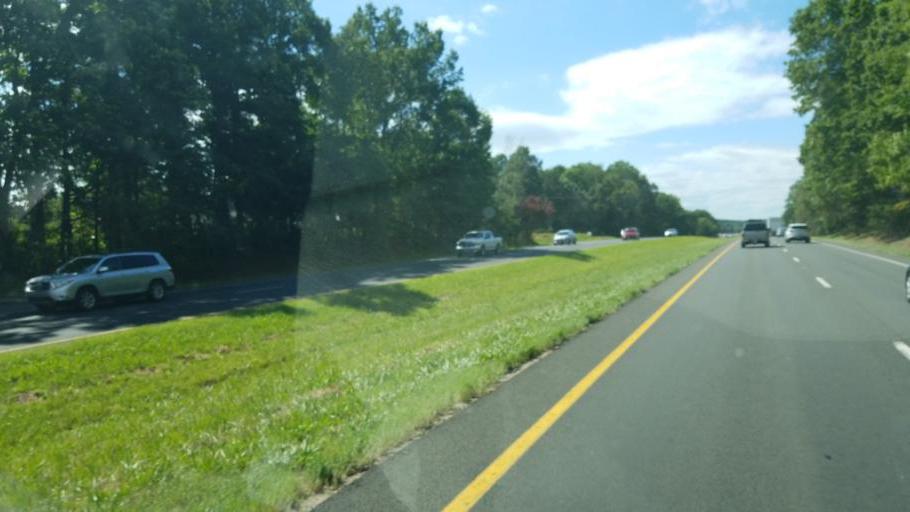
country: US
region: Virginia
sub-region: Fauquier County
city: Bealeton
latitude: 38.4811
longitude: -77.6807
